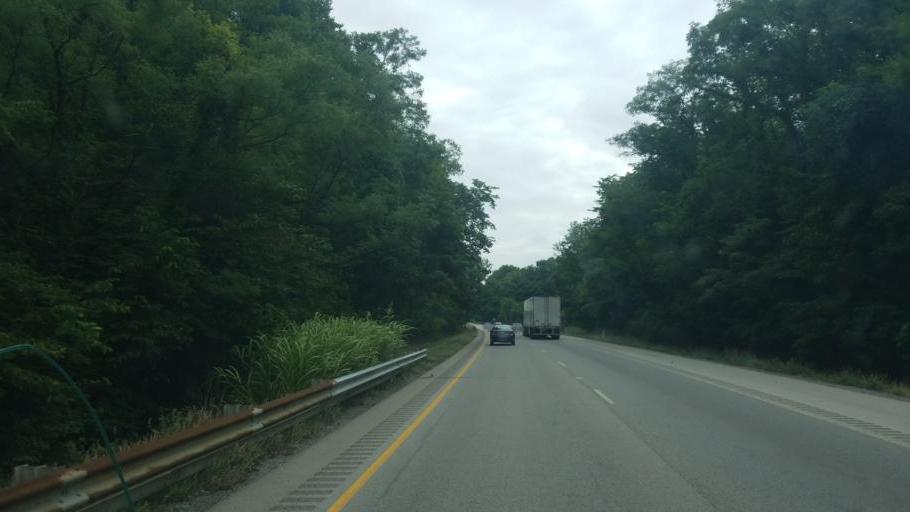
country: US
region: Indiana
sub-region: Putnam County
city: Cloverdale
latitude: 39.5216
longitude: -86.8899
